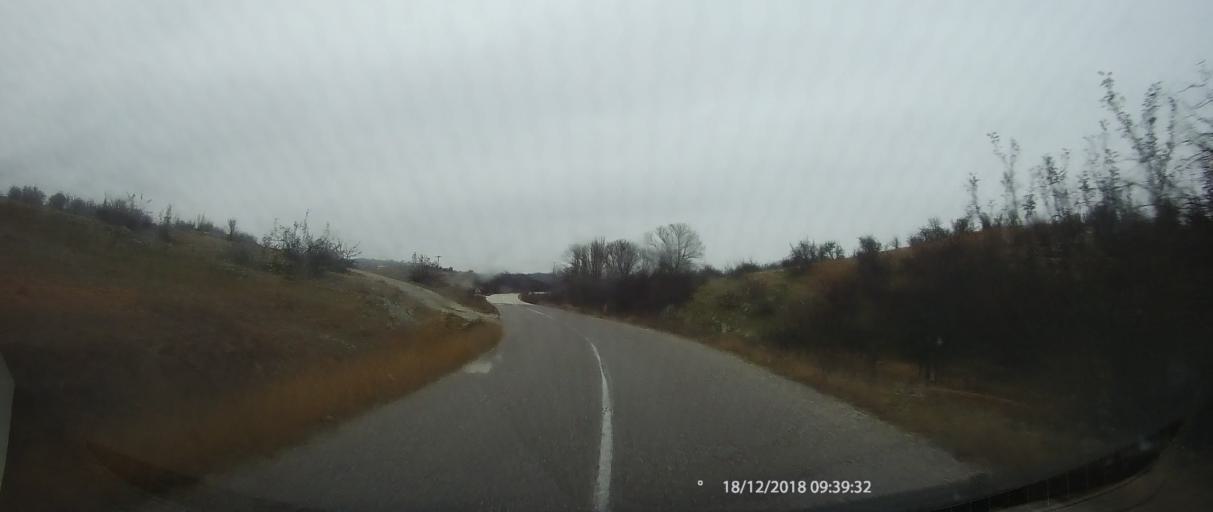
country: GR
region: Thessaly
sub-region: Nomos Larisis
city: Elassona
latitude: 39.9999
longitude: 22.2173
